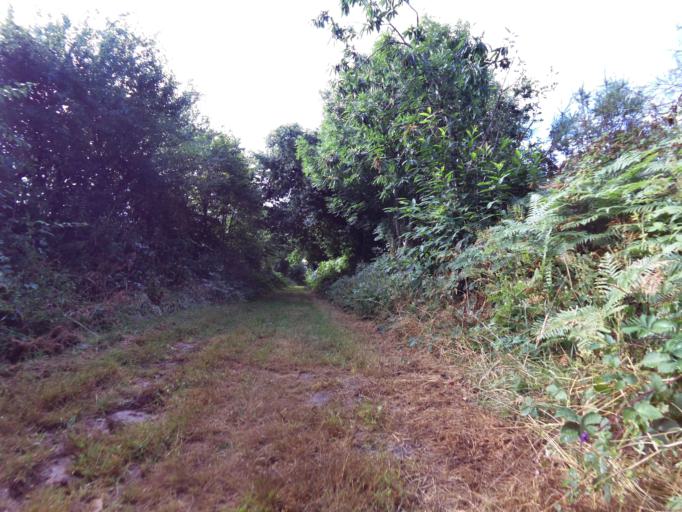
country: FR
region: Brittany
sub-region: Departement d'Ille-et-Vilaine
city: Chanteloup
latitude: 47.9295
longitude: -1.6020
